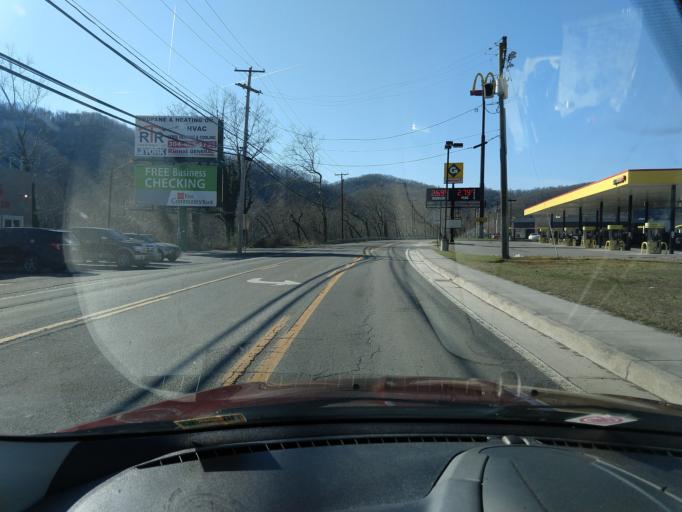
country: US
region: West Virginia
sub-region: Summers County
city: Hinton
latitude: 37.6559
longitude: -80.8869
